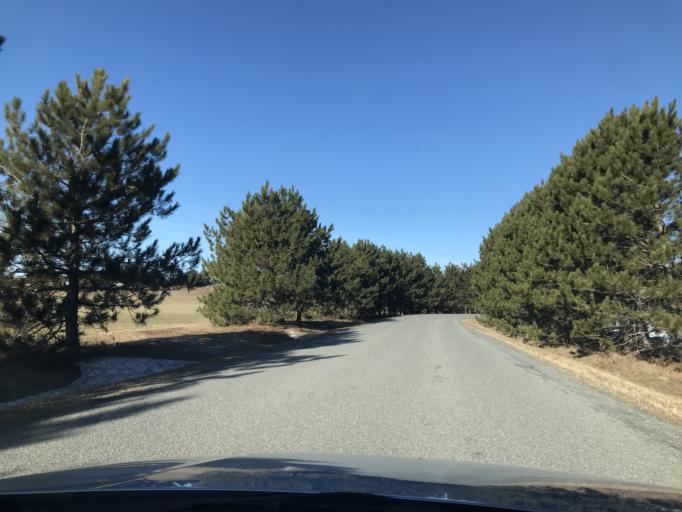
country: US
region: Wisconsin
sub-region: Marinette County
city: Niagara
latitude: 45.3794
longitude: -88.0330
